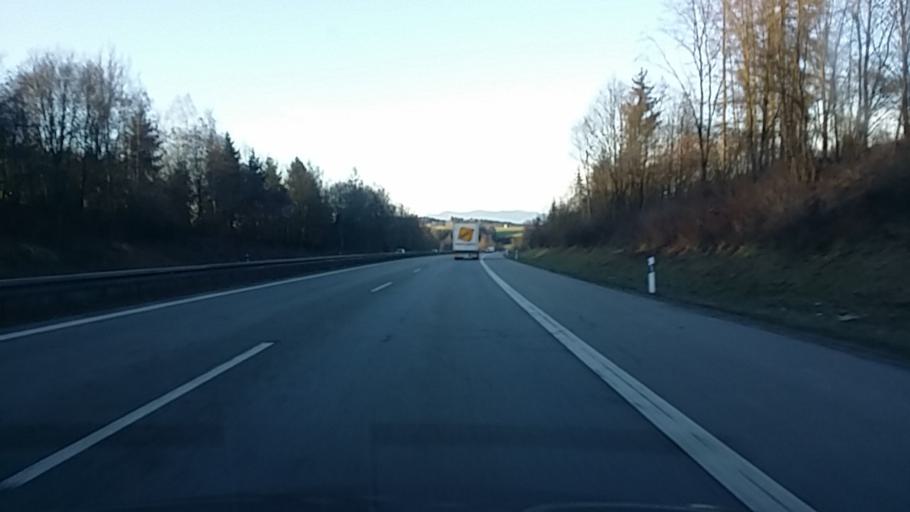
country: DE
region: Bavaria
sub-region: Lower Bavaria
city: Aussernzell
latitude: 48.6954
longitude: 13.1940
